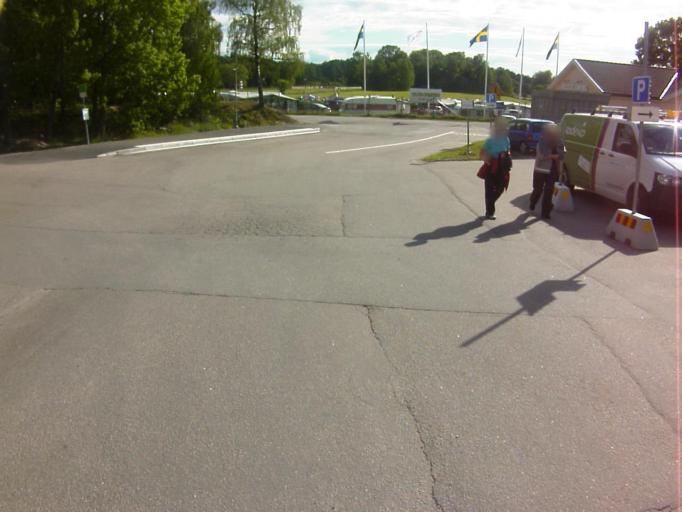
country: SE
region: Soedermanland
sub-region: Eskilstuna Kommun
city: Eskilstuna
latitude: 59.3509
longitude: 16.5100
